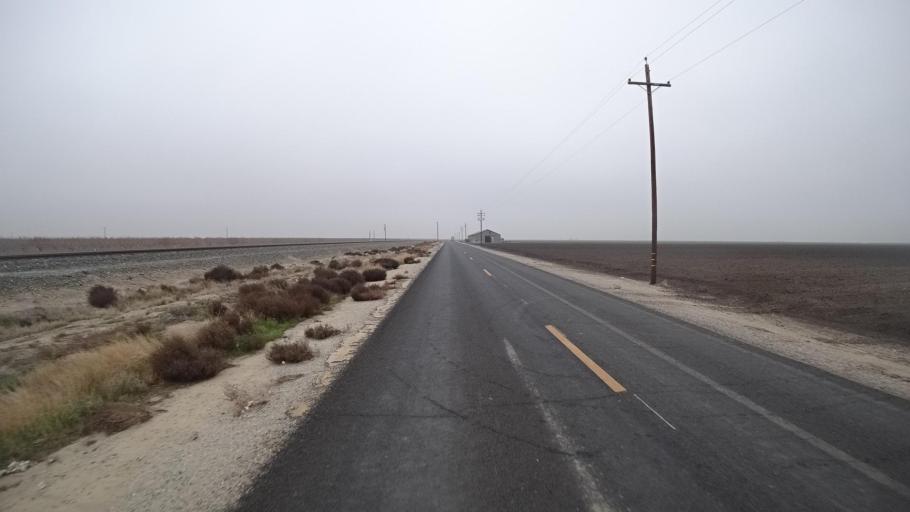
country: US
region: California
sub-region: Kern County
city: Greenfield
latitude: 35.1801
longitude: -119.1703
